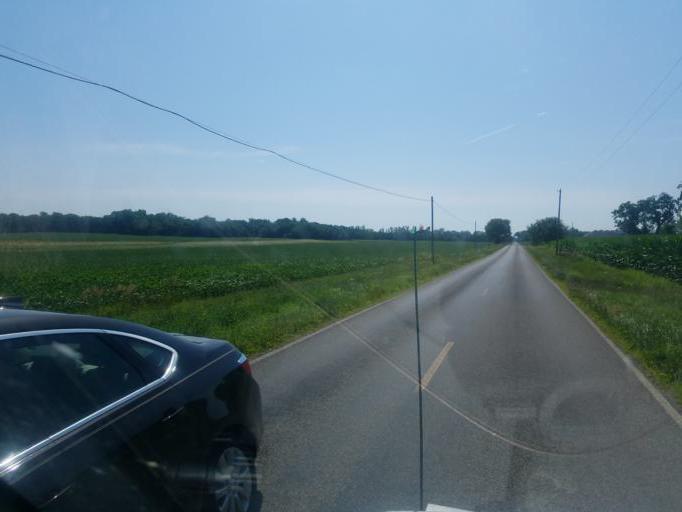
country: US
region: Ohio
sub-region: Champaign County
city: North Lewisburg
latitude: 40.2155
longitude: -83.5077
